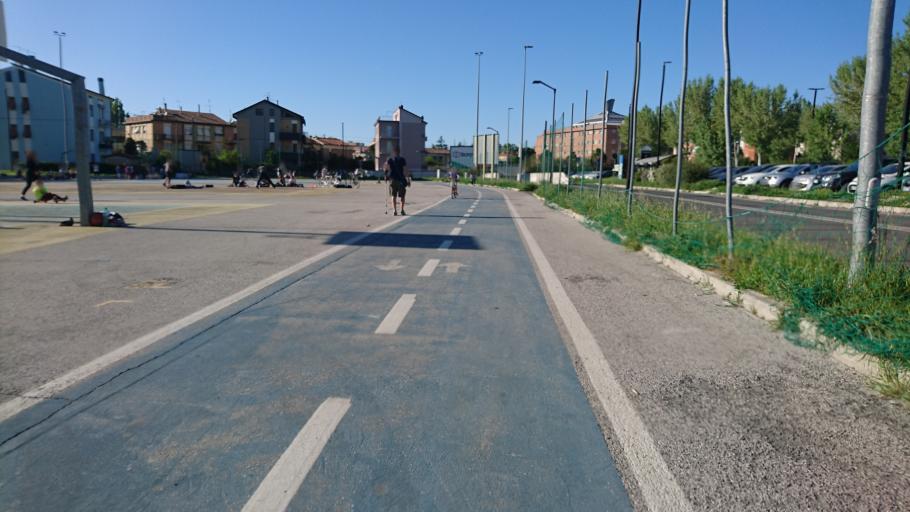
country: IT
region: The Marches
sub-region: Provincia di Pesaro e Urbino
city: Pesaro
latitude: 43.9028
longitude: 12.9135
